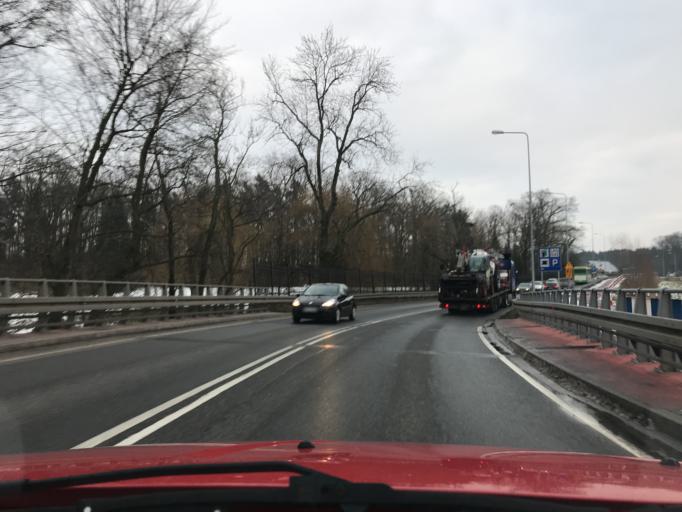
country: PL
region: Greater Poland Voivodeship
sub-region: Powiat pleszewski
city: Goluchow
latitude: 51.8496
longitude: 17.9349
